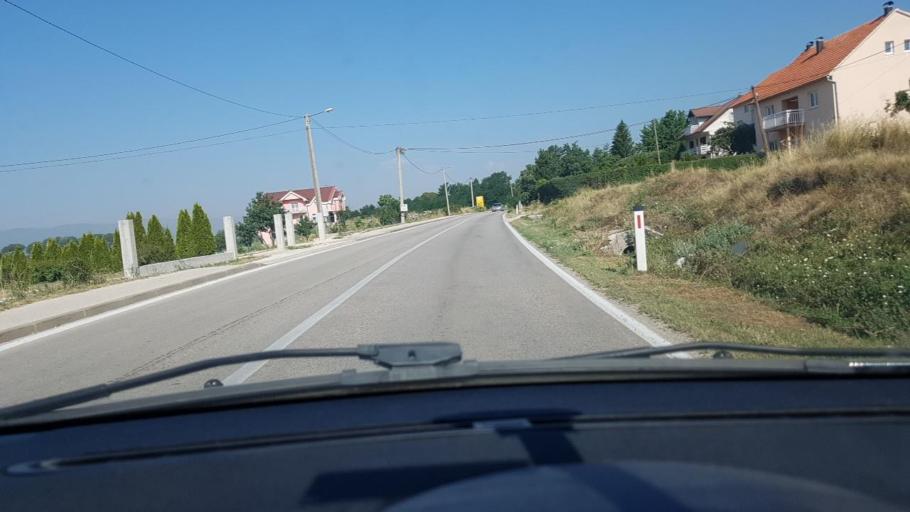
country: BA
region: Federation of Bosnia and Herzegovina
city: Livno
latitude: 43.8314
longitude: 16.9910
